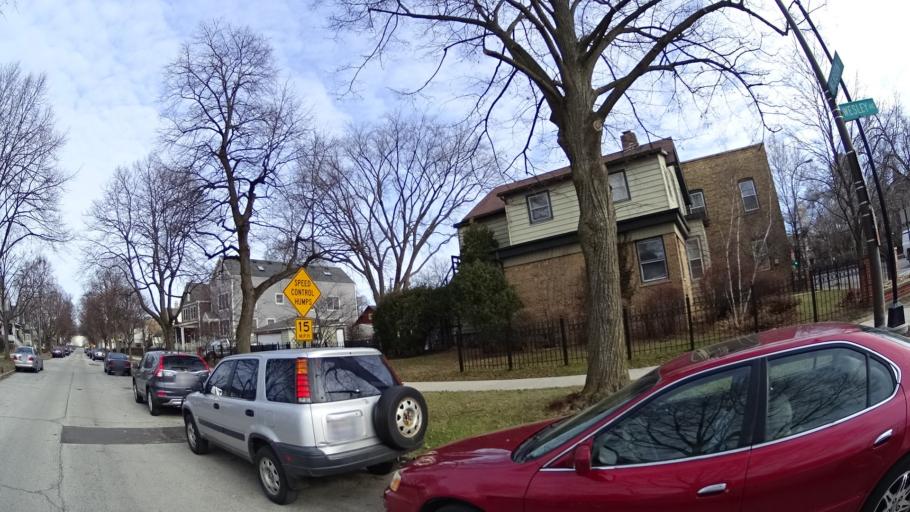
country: US
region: Illinois
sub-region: Cook County
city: Evanston
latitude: 42.0523
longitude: -87.6915
